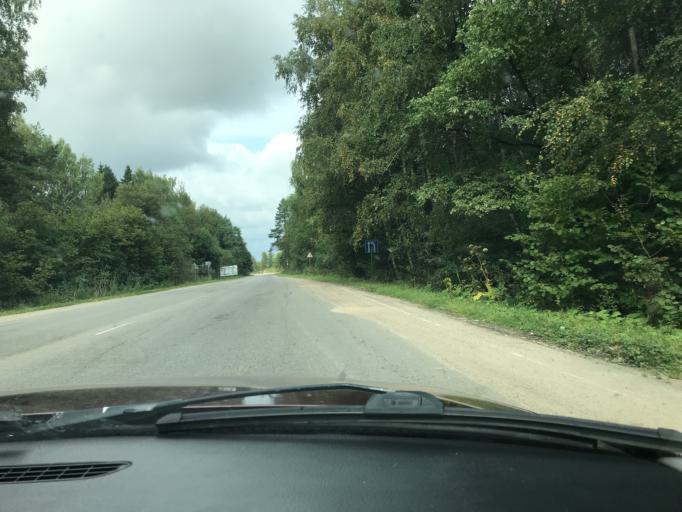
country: RU
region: Kaluga
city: Maloyaroslavets
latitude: 54.9809
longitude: 36.4697
